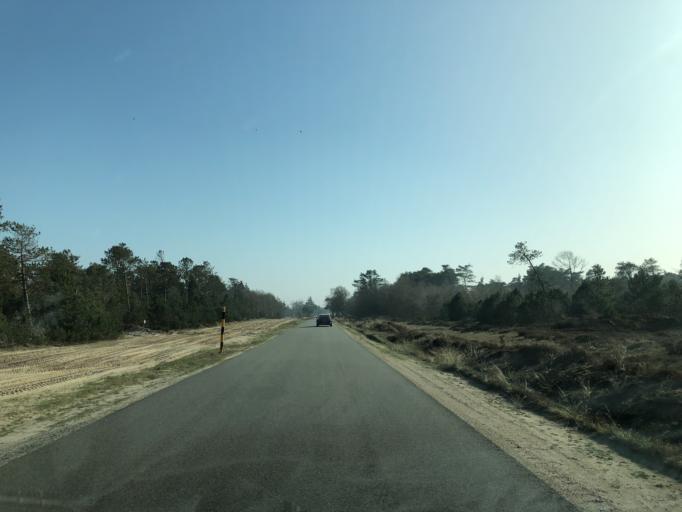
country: DK
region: South Denmark
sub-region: Varde Kommune
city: Oksbol
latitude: 55.6307
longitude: 8.1713
